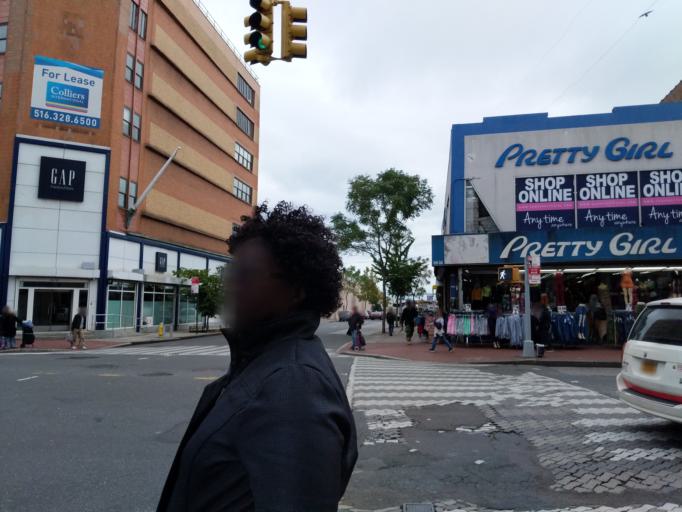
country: US
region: New York
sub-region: Queens County
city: Jamaica
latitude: 40.7059
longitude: -73.7940
